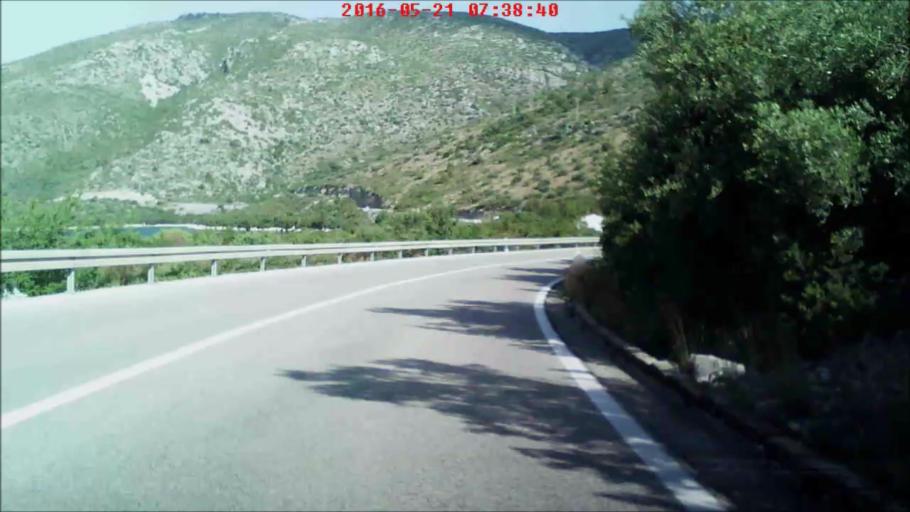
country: HR
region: Dubrovacko-Neretvanska
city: Podgora
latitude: 42.8017
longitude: 17.8482
